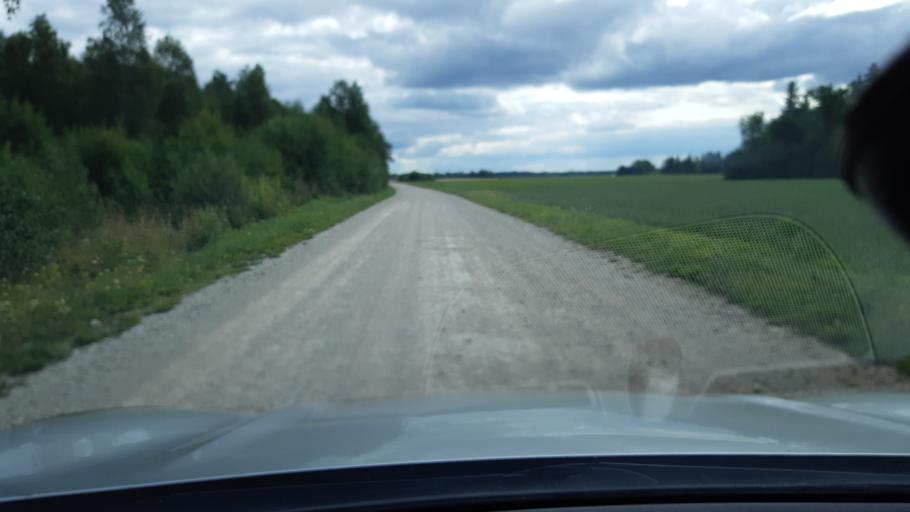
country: EE
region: Paernumaa
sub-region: Vaendra vald (alev)
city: Vandra
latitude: 58.7880
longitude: 25.0230
